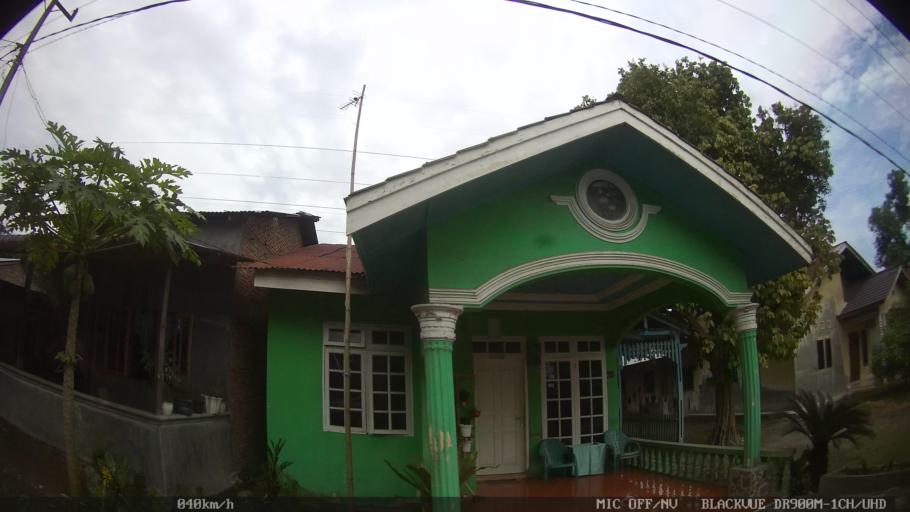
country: ID
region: North Sumatra
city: Sunggal
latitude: 3.6608
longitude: 98.5885
